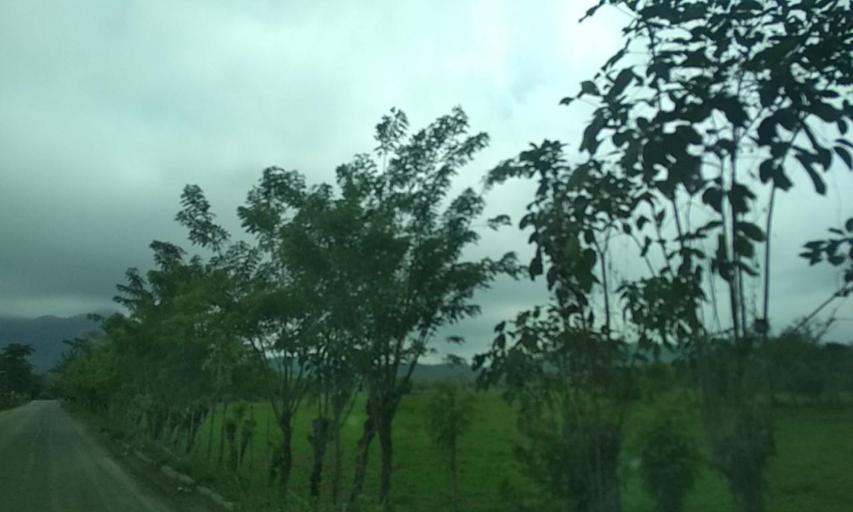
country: MX
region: Veracruz
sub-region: Uxpanapa
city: Poblado 10
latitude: 17.5054
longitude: -94.1607
